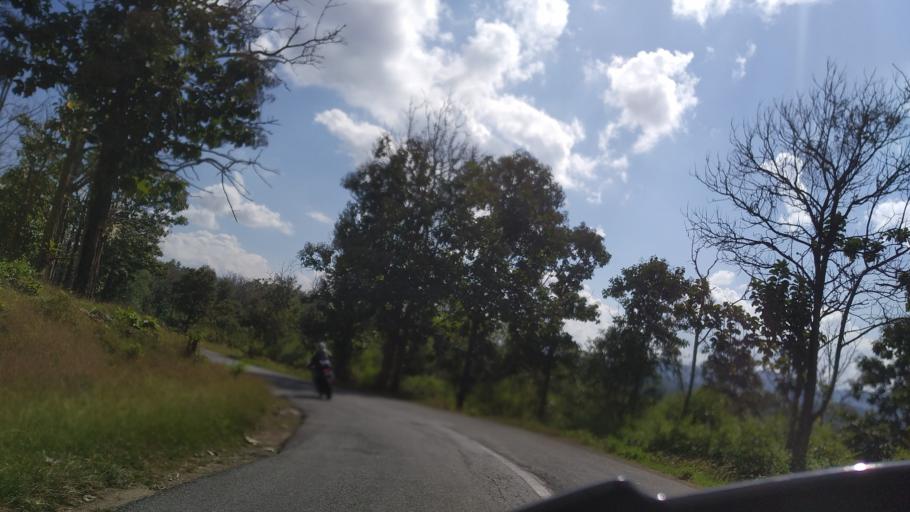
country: IN
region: Kerala
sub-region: Wayanad
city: Panamaram
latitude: 11.9214
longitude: 76.0664
